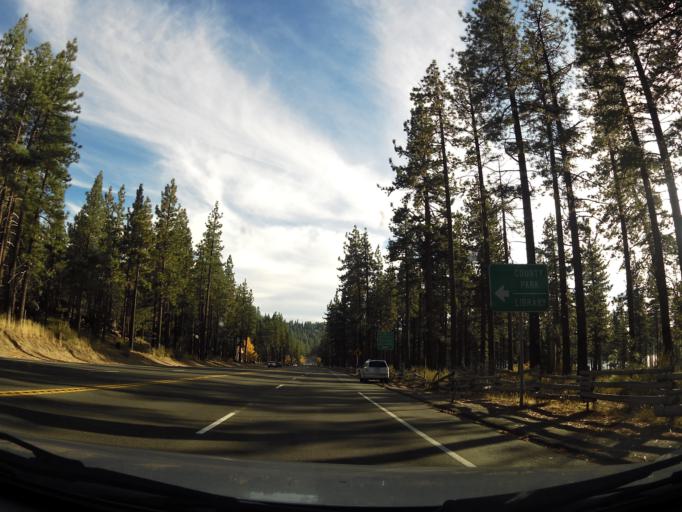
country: US
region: Nevada
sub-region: Douglas County
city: Kingsbury
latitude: 39.0136
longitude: -119.9476
